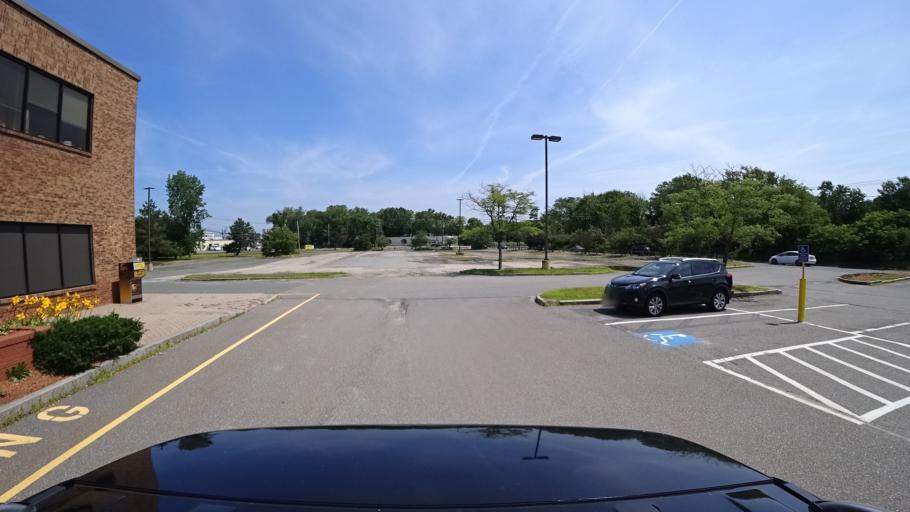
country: US
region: Massachusetts
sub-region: Norfolk County
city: Dedham
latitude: 42.2437
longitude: -71.1722
